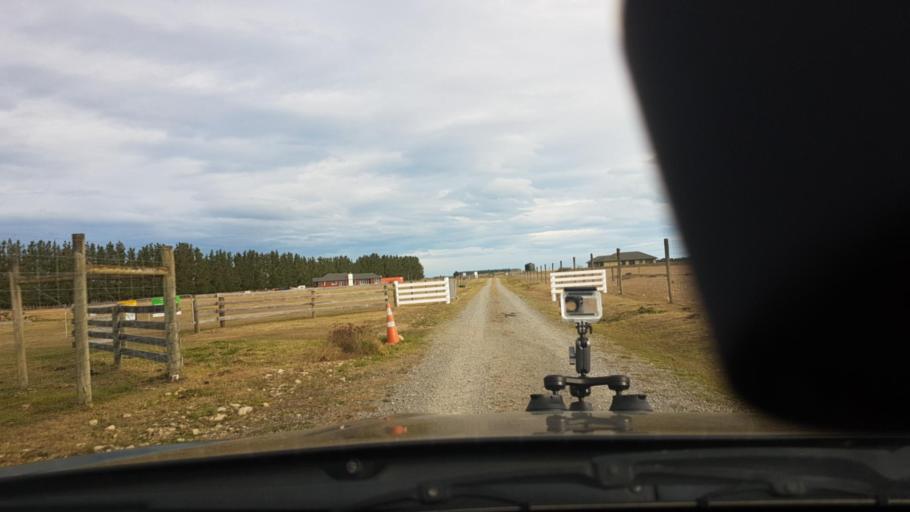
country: NZ
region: Canterbury
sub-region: Waimakariri District
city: Oxford
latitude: -43.3998
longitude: 172.3125
